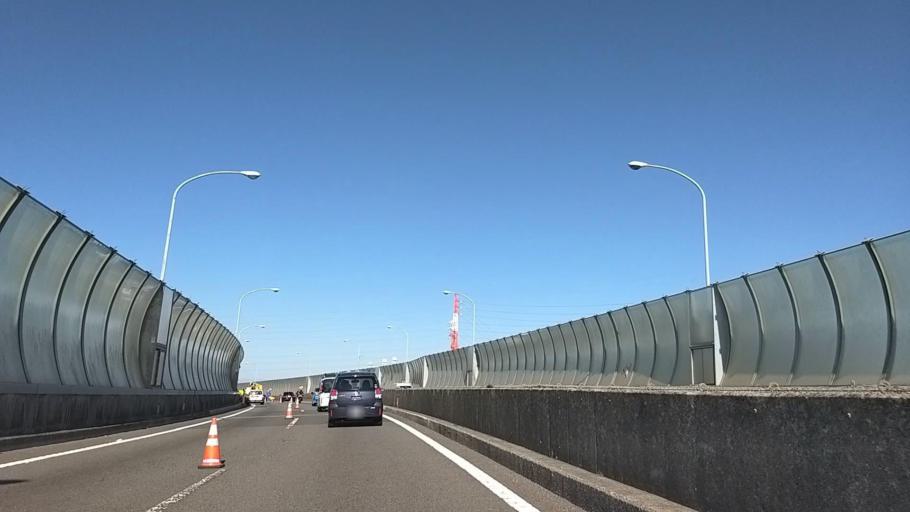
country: JP
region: Kanagawa
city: Minami-rinkan
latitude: 35.5013
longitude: 139.4909
